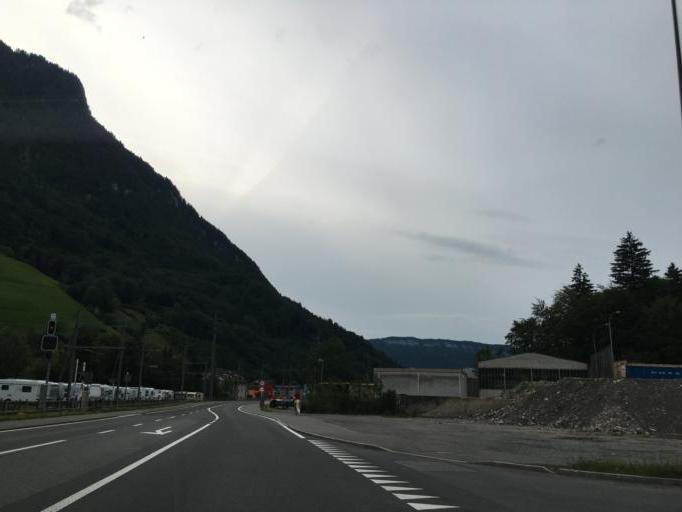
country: CH
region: Nidwalden
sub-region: Nidwalden
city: Dallenwil
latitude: 46.9295
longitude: 8.3945
